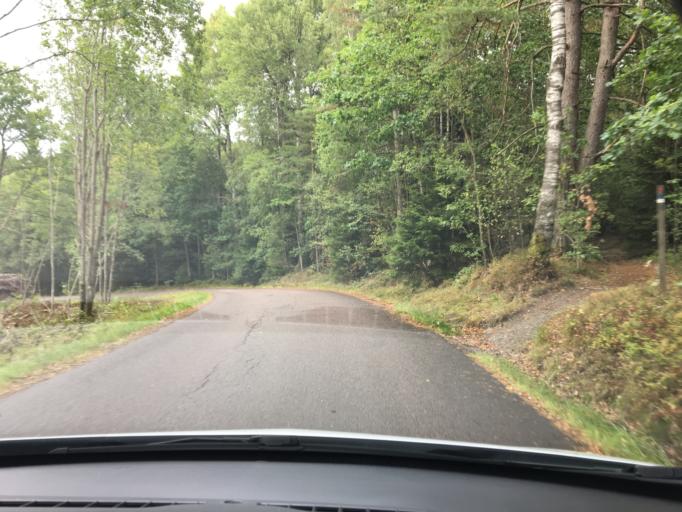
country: SE
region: Vaestra Goetaland
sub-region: Ale Kommun
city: Nodinge-Nol
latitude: 57.8798
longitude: 12.0837
